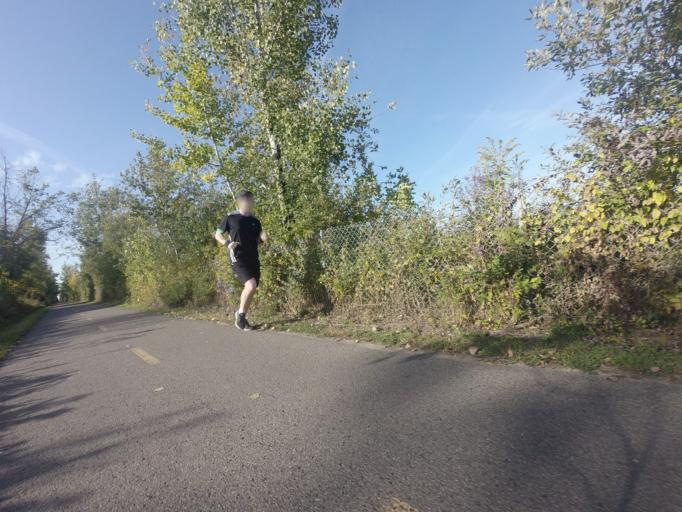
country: CA
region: Quebec
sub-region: Laurentides
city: Blainville
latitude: 45.7262
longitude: -73.9377
